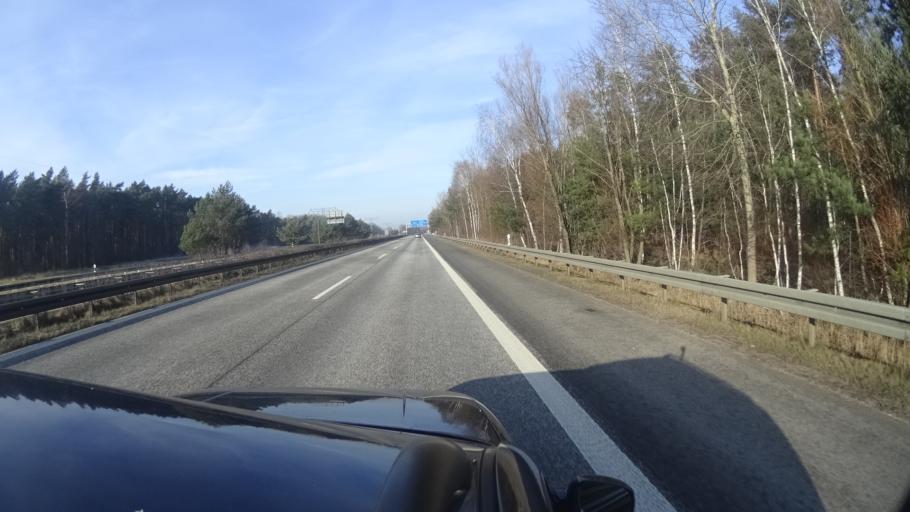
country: DE
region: Brandenburg
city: Velten
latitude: 52.6840
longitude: 13.2160
